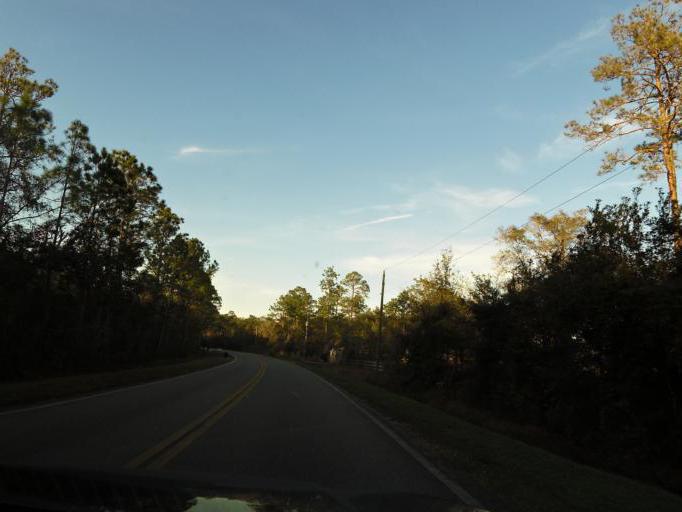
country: US
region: Florida
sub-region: Clay County
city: Green Cove Springs
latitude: 29.8653
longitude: -81.5448
